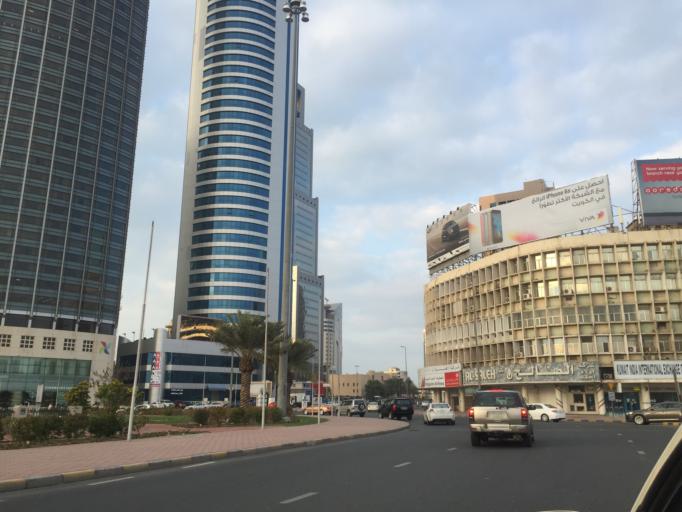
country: KW
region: Al Asimah
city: Ash Shamiyah
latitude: 29.3606
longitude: 47.9641
